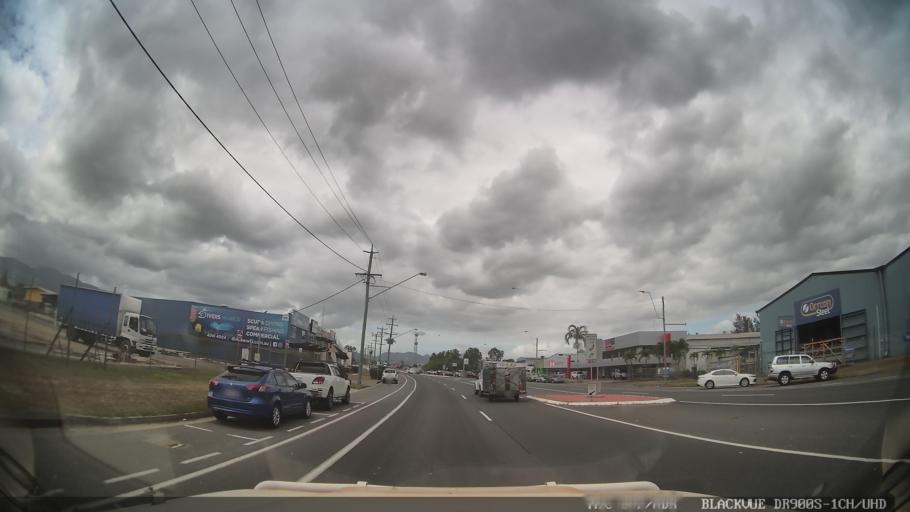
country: AU
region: Queensland
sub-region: Cairns
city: Cairns
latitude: -16.9394
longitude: 145.7653
